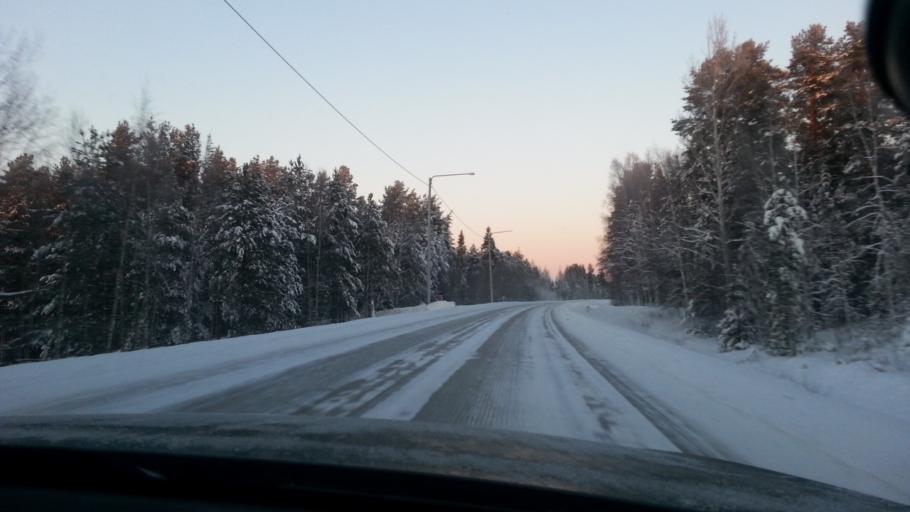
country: FI
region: Lapland
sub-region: Tunturi-Lappi
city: Kittilae
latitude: 67.0443
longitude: 25.0945
